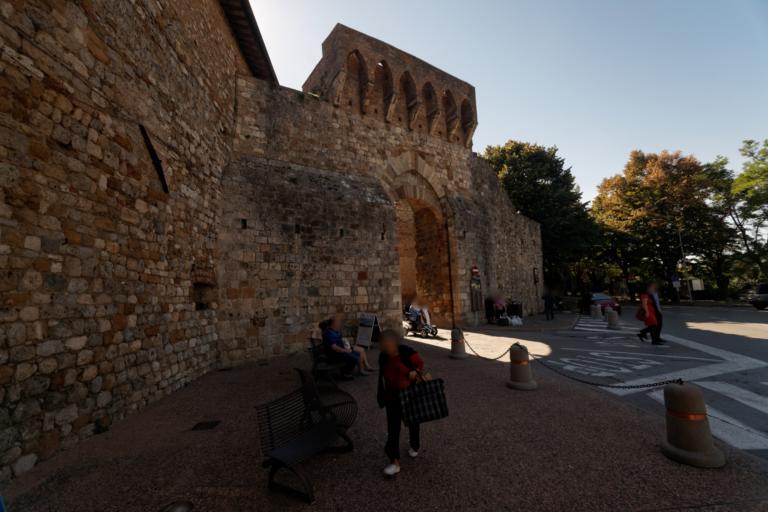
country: IT
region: Tuscany
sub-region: Provincia di Siena
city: San Gimignano
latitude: 43.4701
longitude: 11.0411
